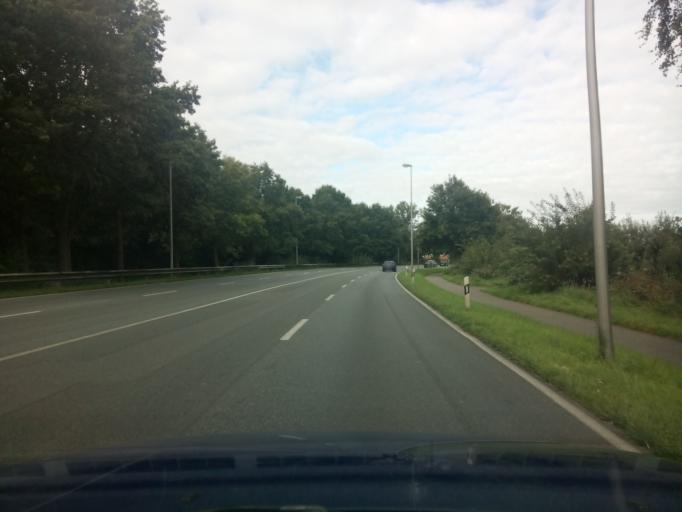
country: DE
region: Lower Saxony
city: Lilienthal
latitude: 53.1111
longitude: 8.8824
